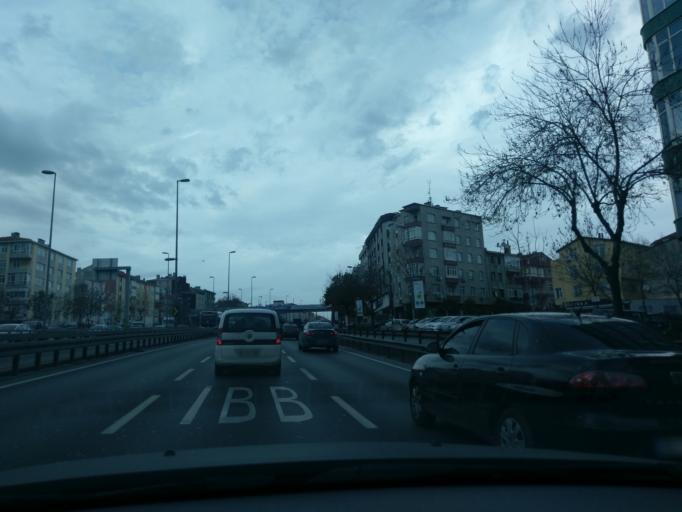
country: TR
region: Istanbul
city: Yakuplu
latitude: 40.9782
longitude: 28.7359
